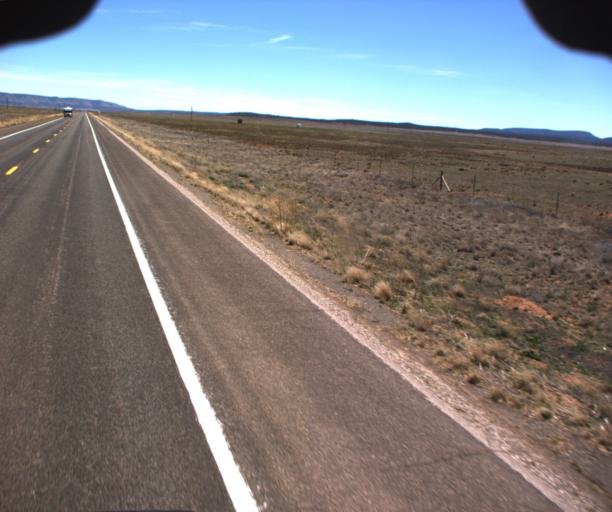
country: US
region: Arizona
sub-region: Mohave County
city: Peach Springs
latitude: 35.4706
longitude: -113.1256
